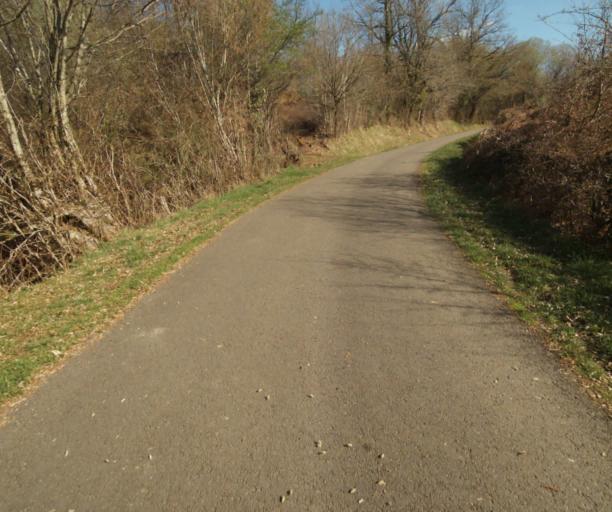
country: FR
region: Limousin
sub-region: Departement de la Correze
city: Saint-Mexant
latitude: 45.3217
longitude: 1.6199
